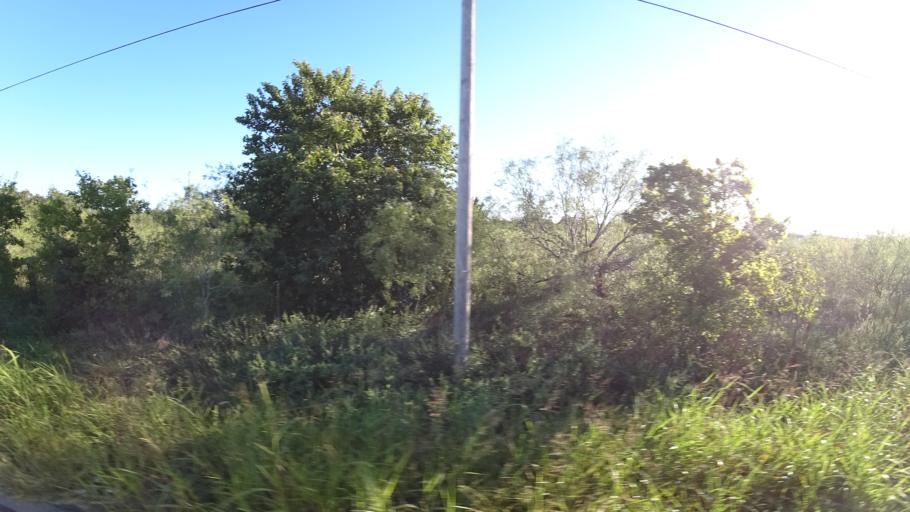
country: US
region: Texas
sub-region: Travis County
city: Manor
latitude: 30.3156
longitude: -97.6225
